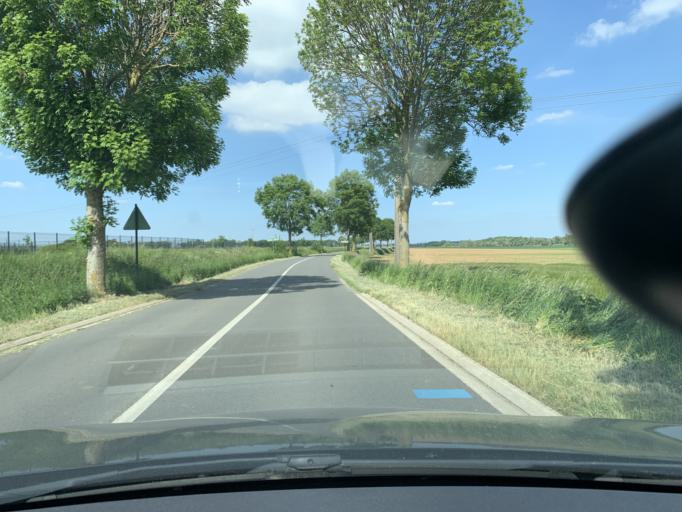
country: FR
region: Nord-Pas-de-Calais
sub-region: Departement du Pas-de-Calais
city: Marquion
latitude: 50.2171
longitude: 3.0687
